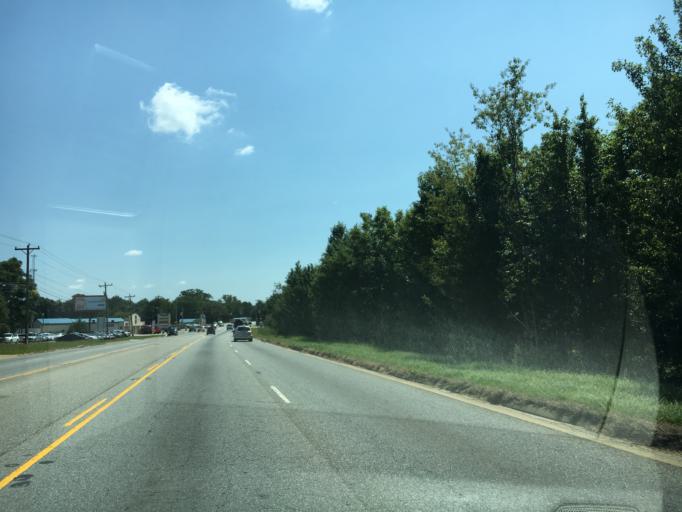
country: US
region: South Carolina
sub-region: Spartanburg County
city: Duncan
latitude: 34.8850
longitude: -82.1521
